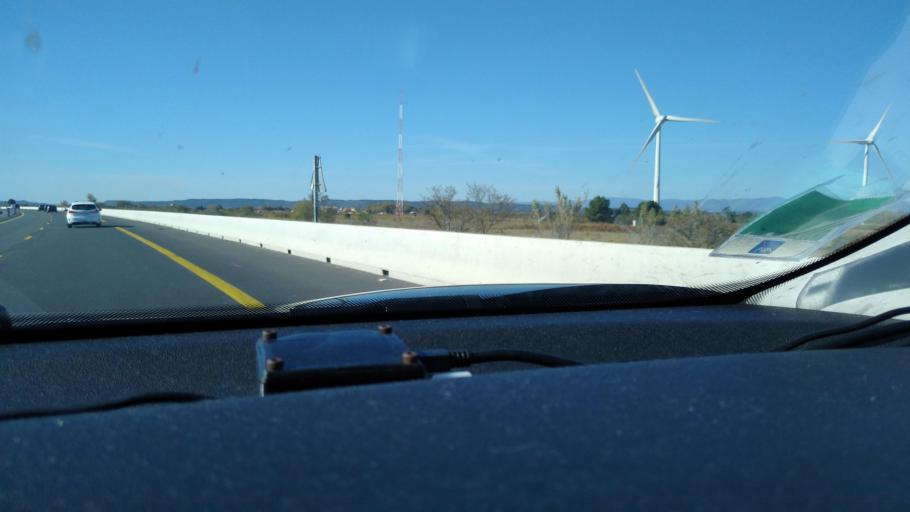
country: FR
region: Languedoc-Roussillon
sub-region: Departement de l'Aude
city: Ornaisons
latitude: 43.1713
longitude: 2.8035
